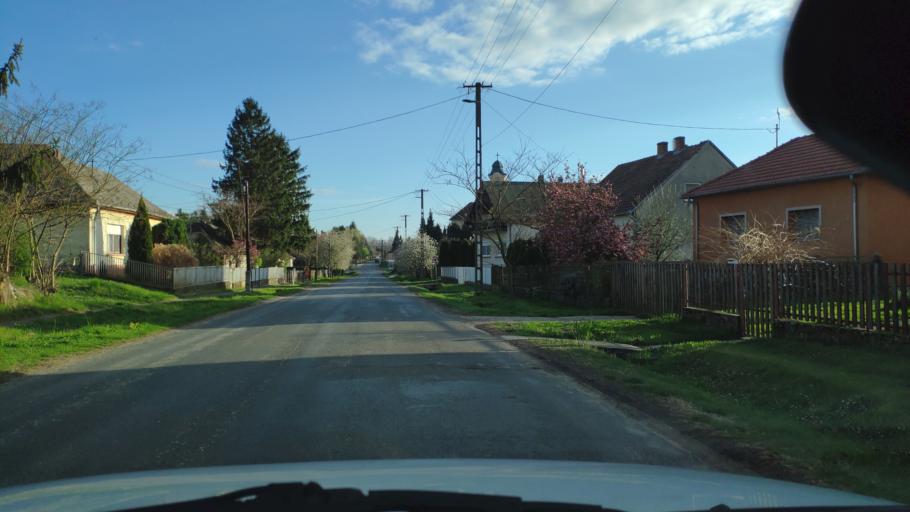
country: HU
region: Zala
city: Zalakomar
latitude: 46.4545
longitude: 17.1257
